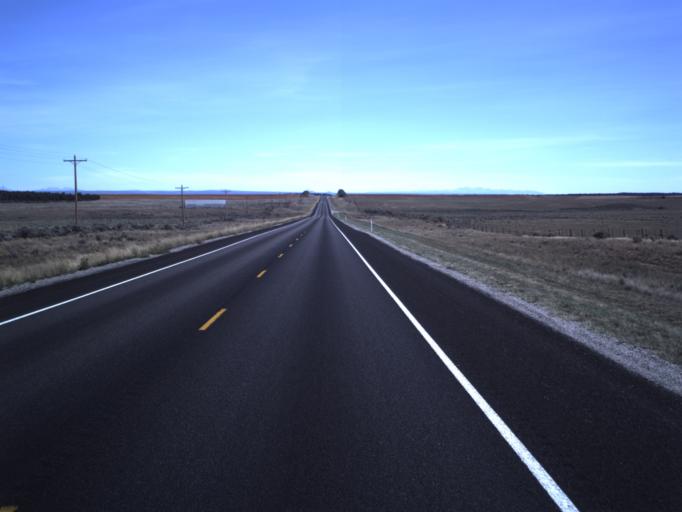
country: US
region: Utah
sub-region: San Juan County
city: Monticello
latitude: 37.8513
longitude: -109.1699
